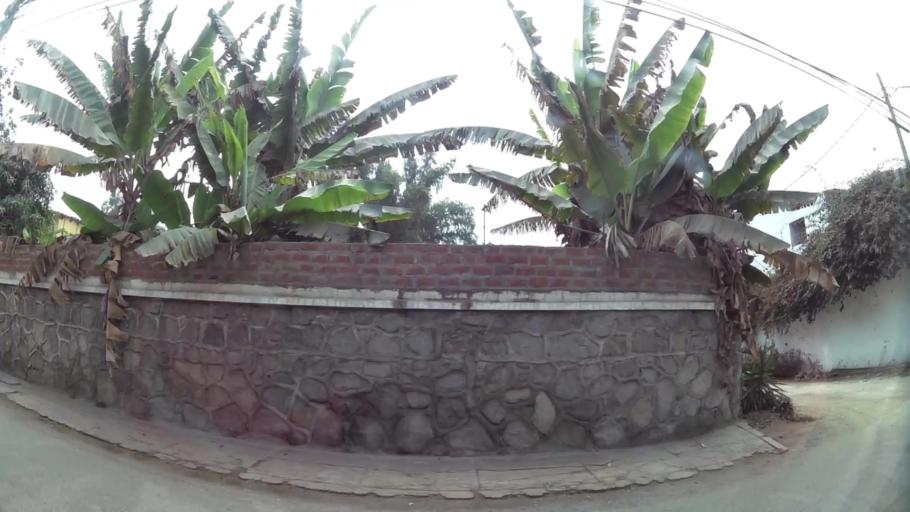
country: PE
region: Lima
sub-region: Lima
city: Chaclacayo
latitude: -11.9798
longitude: -76.7744
